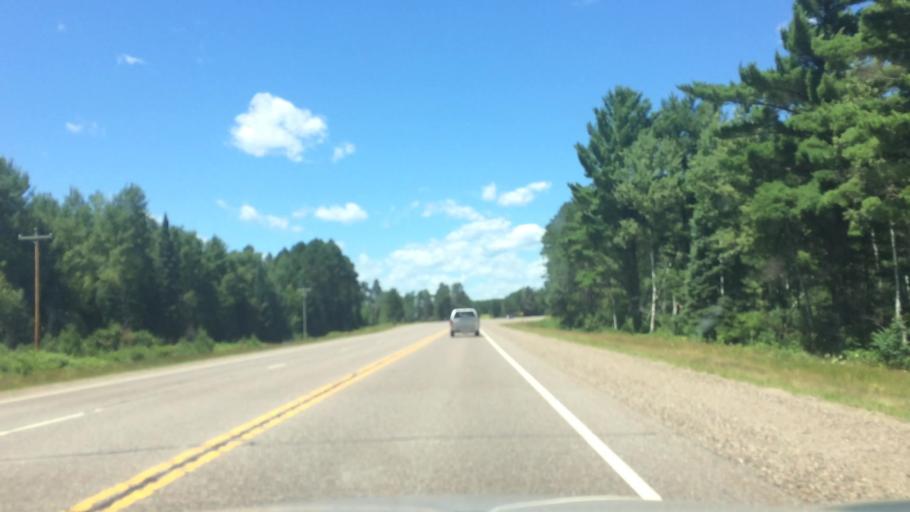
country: US
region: Wisconsin
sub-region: Lincoln County
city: Tomahawk
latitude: 45.6617
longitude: -89.7105
